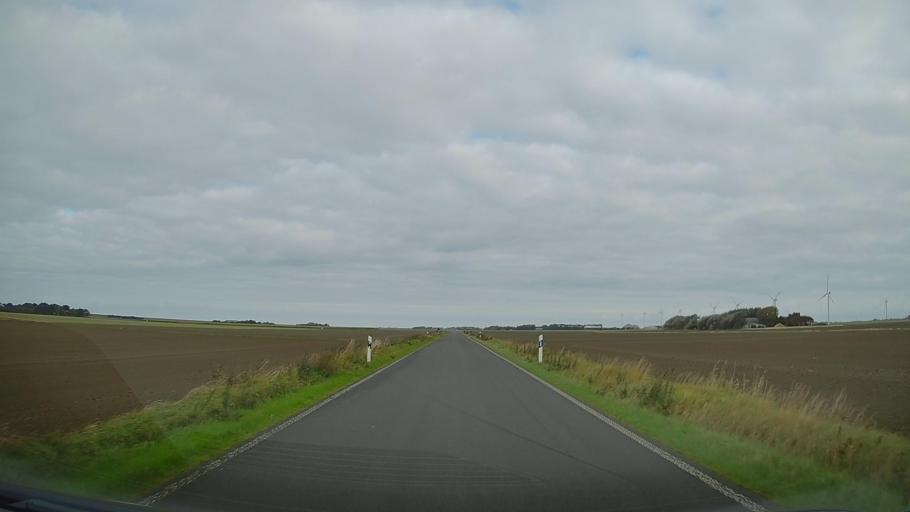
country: DE
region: Schleswig-Holstein
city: Friedrich-Wilhelm-Lubke-Koog
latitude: 54.8457
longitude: 8.6223
